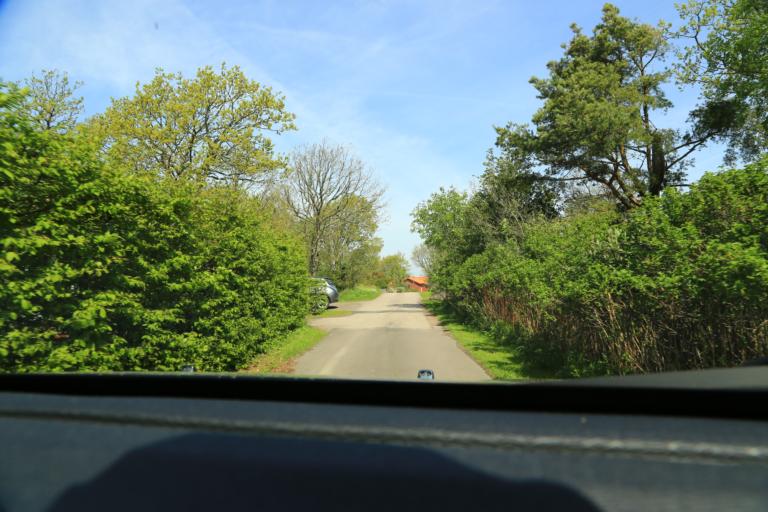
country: SE
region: Halland
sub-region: Varbergs Kommun
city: Varberg
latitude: 57.1361
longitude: 12.2227
